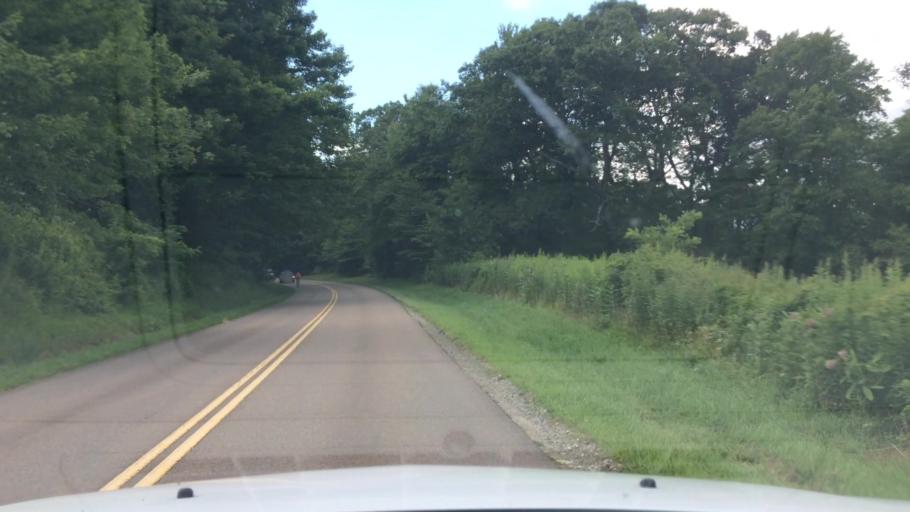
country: US
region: North Carolina
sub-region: Watauga County
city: Blowing Rock
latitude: 36.1532
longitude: -81.6672
